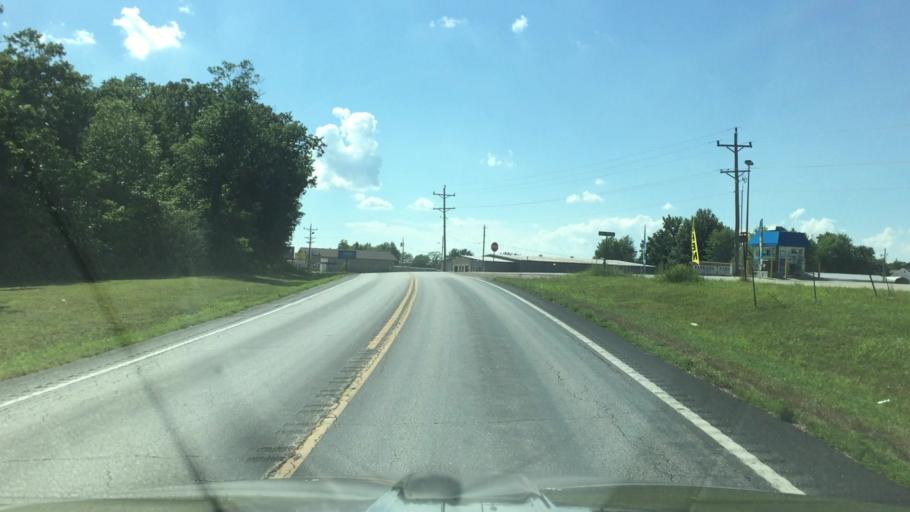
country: US
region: Missouri
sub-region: Camden County
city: Osage Beach
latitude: 38.1394
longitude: -92.5810
